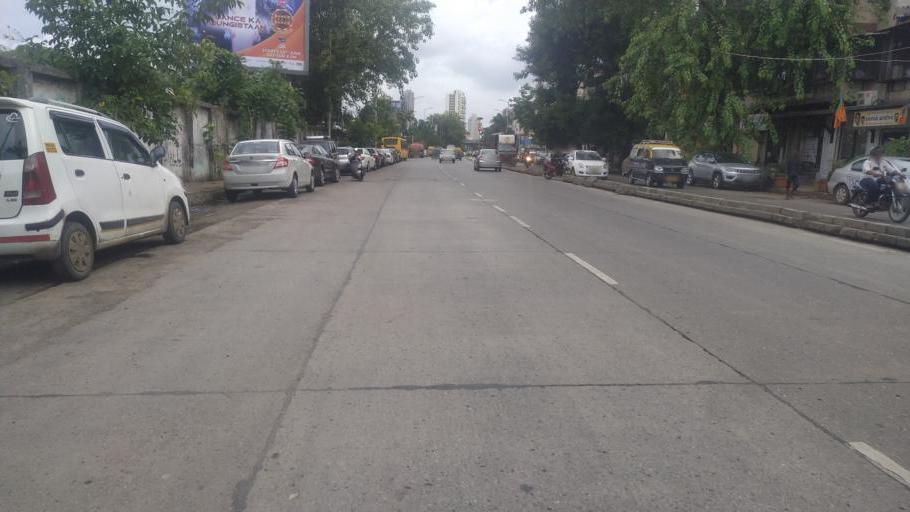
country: IN
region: Maharashtra
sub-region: Mumbai Suburban
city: Mumbai
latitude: 19.0335
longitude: 72.8478
